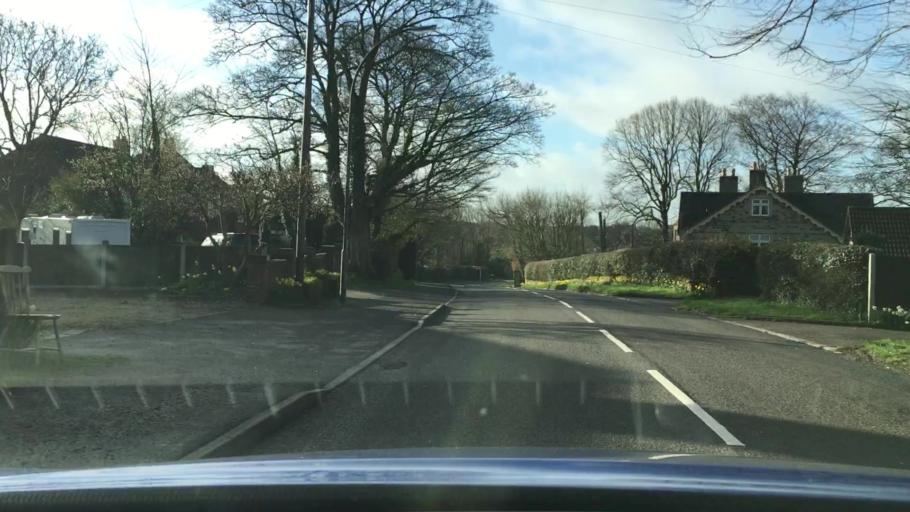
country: GB
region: England
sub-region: Derbyshire
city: Tibshelf
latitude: 53.1523
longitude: -1.3369
